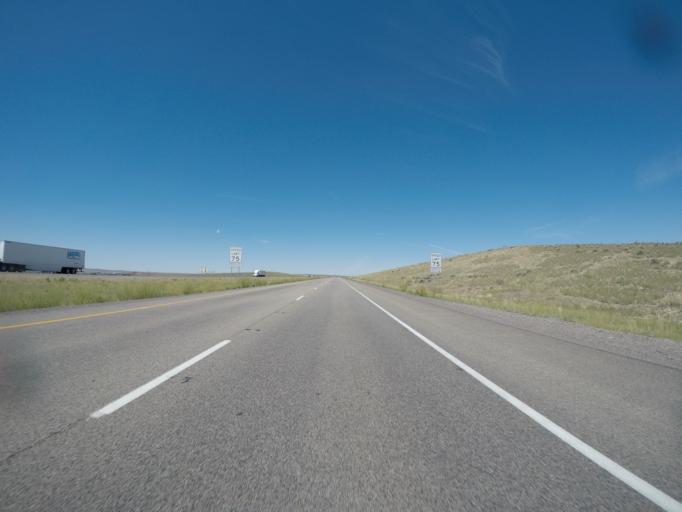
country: US
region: Wyoming
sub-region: Carbon County
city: Saratoga
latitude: 41.7429
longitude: -106.7823
